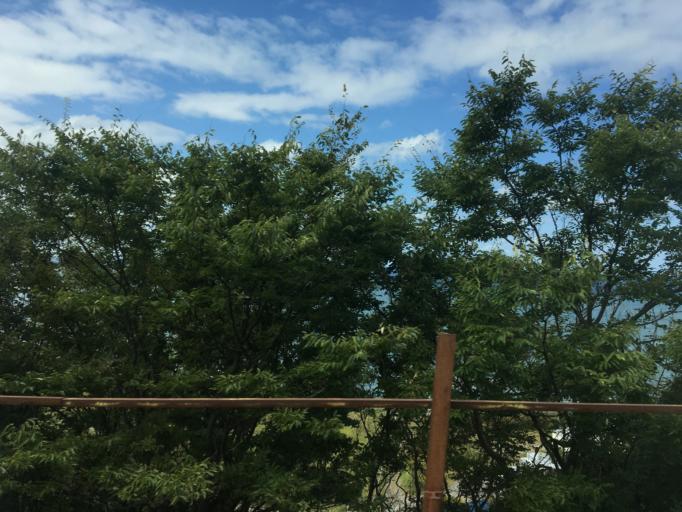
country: JP
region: Aomori
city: Shimokizukuri
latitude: 40.7757
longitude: 140.1877
